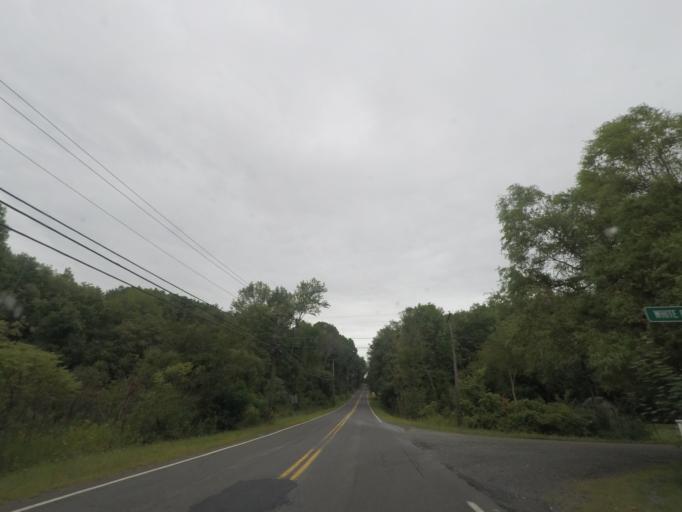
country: US
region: New York
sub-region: Rensselaer County
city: Nassau
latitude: 42.4453
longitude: -73.5662
